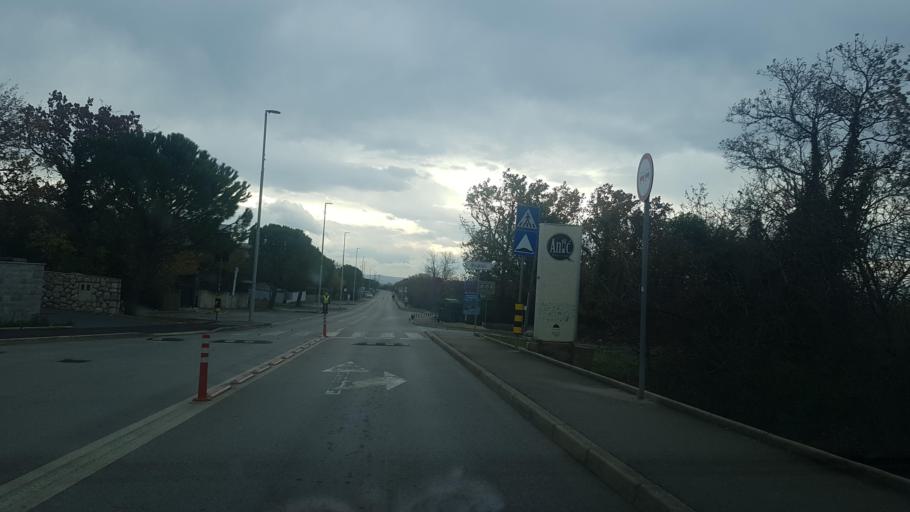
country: HR
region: Primorsko-Goranska
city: Skrljevo
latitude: 45.3043
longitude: 14.4901
